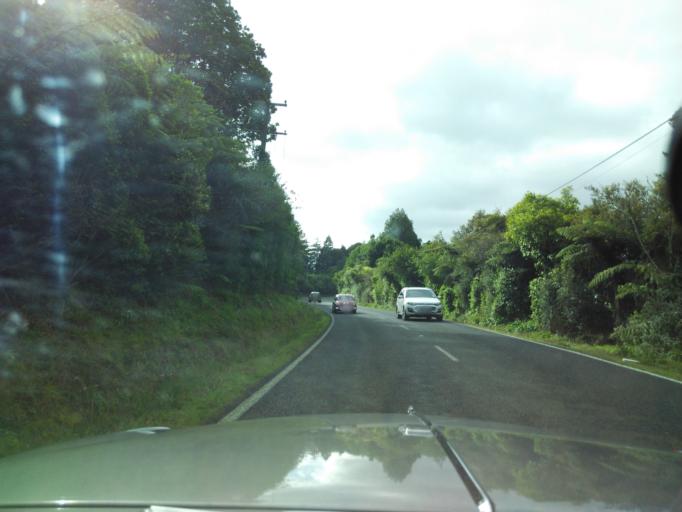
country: NZ
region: Auckland
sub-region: Auckland
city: Red Hill
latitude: -37.1287
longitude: 175.0517
